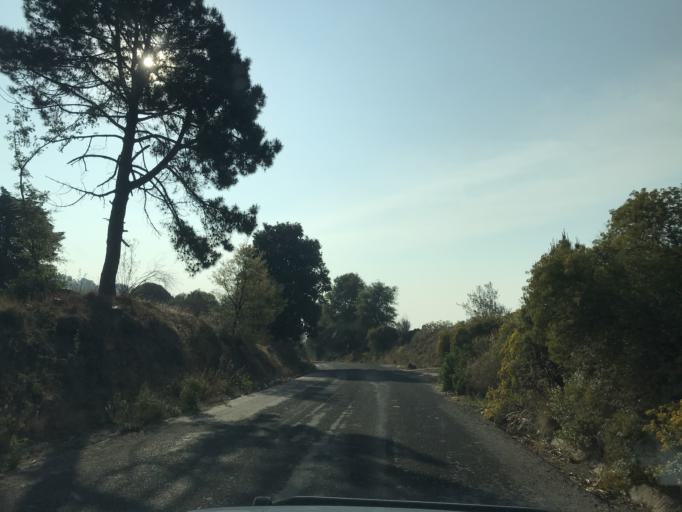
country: MX
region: Puebla
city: San Nicolas de los Ranchos
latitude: 19.0861
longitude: -98.5280
